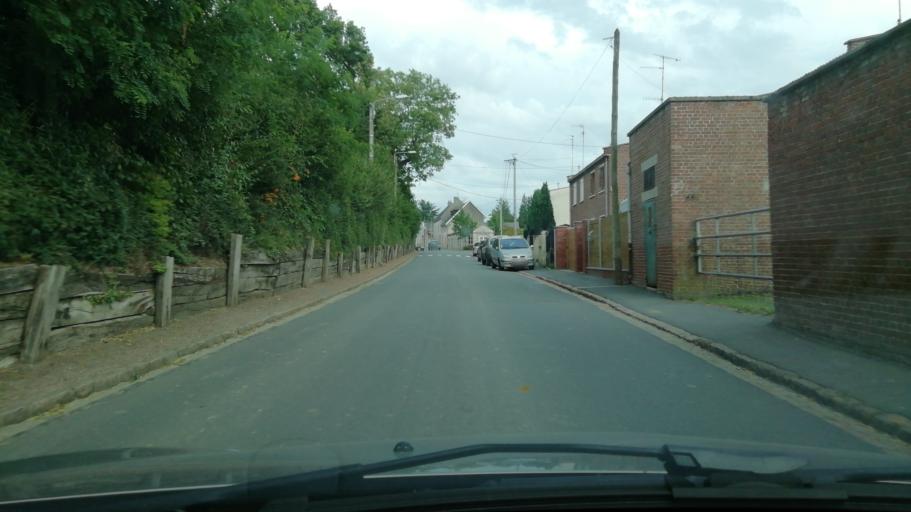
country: FR
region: Nord-Pas-de-Calais
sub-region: Departement du Nord
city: Rieux-en-Cambresis
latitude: 50.1653
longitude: 3.3492
